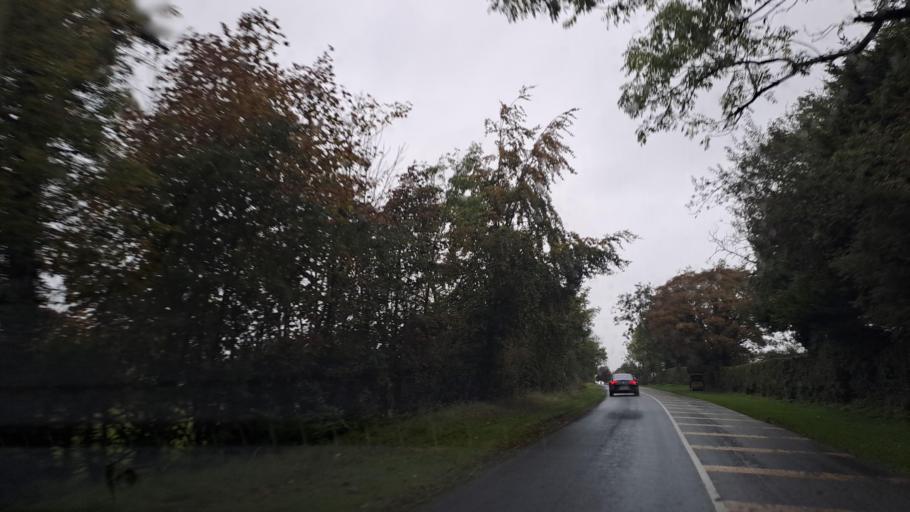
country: IE
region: Ulster
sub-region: County Monaghan
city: Monaghan
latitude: 54.2137
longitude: -6.9069
